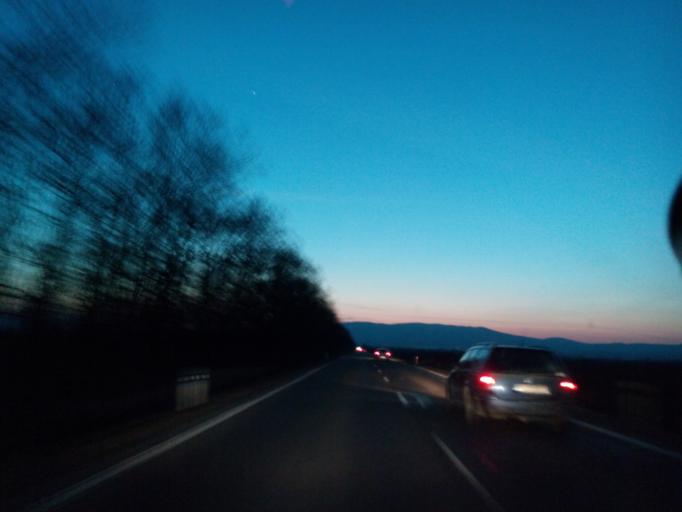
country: SK
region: Kosicky
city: Trebisov
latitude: 48.7003
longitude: 21.7364
